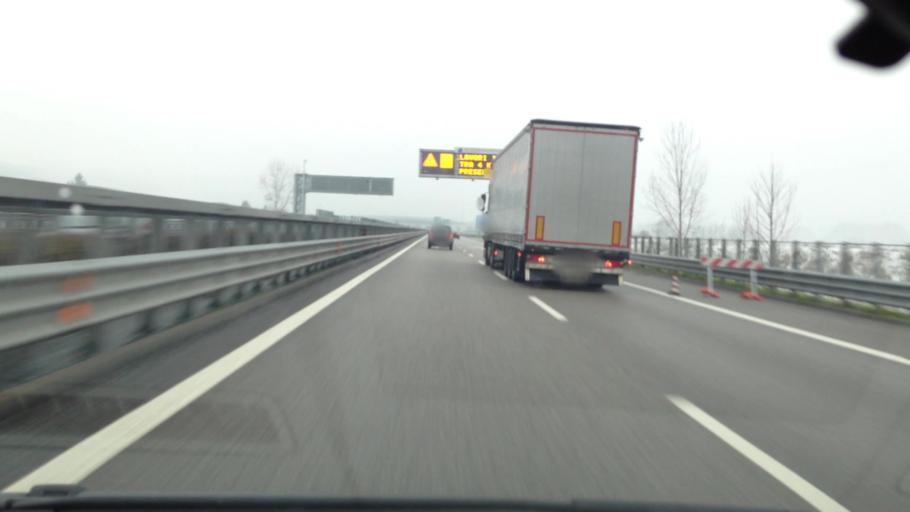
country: IT
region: Piedmont
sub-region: Provincia di Asti
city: Mongardino
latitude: 44.8532
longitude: 8.1969
